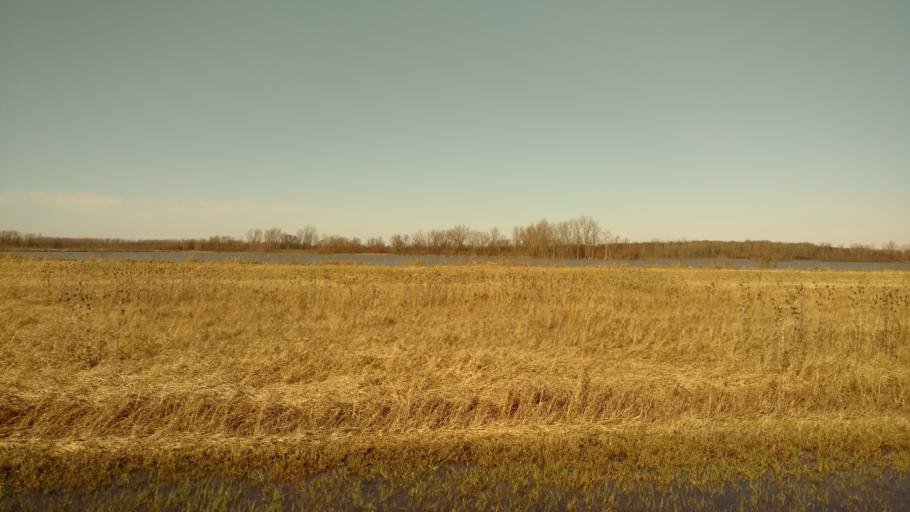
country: US
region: Ohio
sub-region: Wyandot County
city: Upper Sandusky
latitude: 40.7021
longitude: -83.2803
